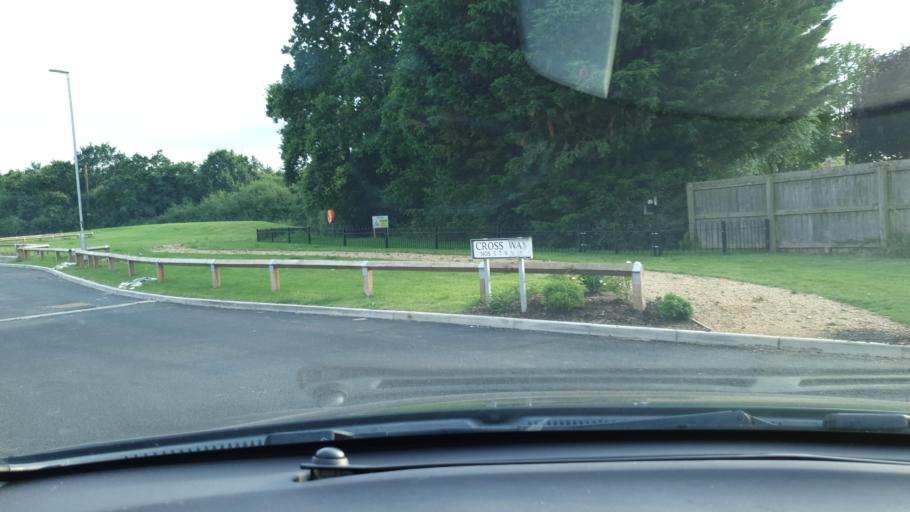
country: GB
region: England
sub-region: Essex
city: Little Clacton
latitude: 51.8585
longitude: 1.1725
